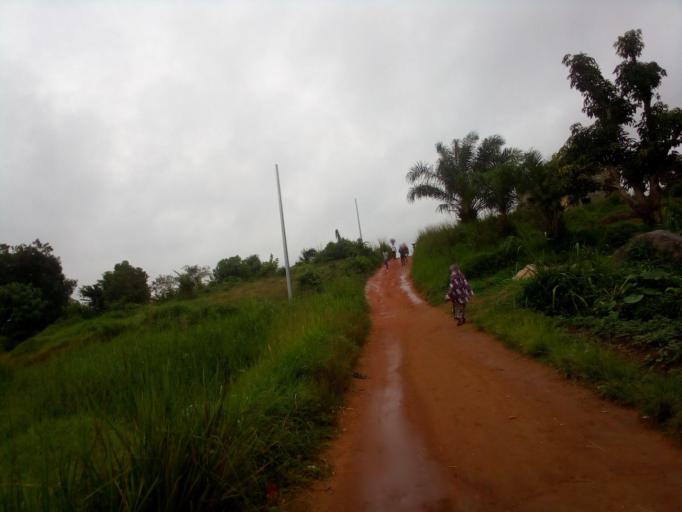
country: SL
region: Eastern Province
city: Kailahun
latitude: 8.2759
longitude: -10.5833
